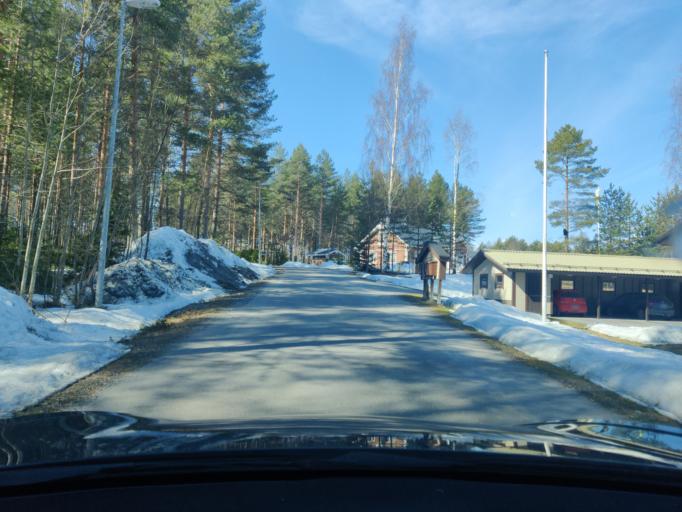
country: FI
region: Northern Savo
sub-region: Kuopio
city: Vehmersalmi
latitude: 62.7702
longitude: 27.9915
